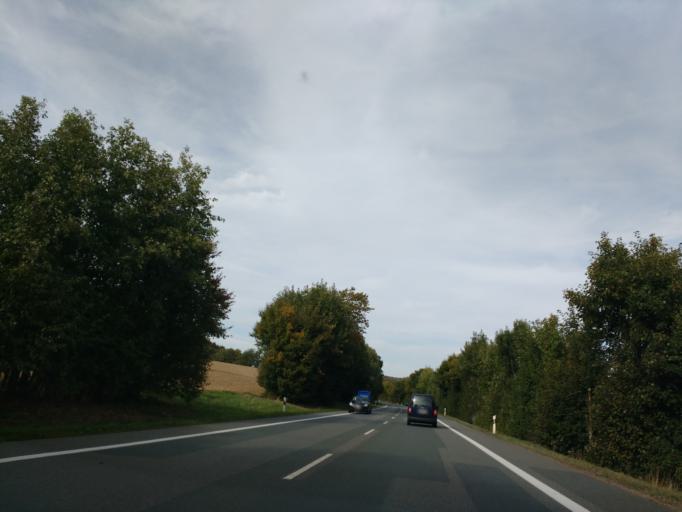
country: DE
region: North Rhine-Westphalia
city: Brakel
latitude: 51.7440
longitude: 9.1747
